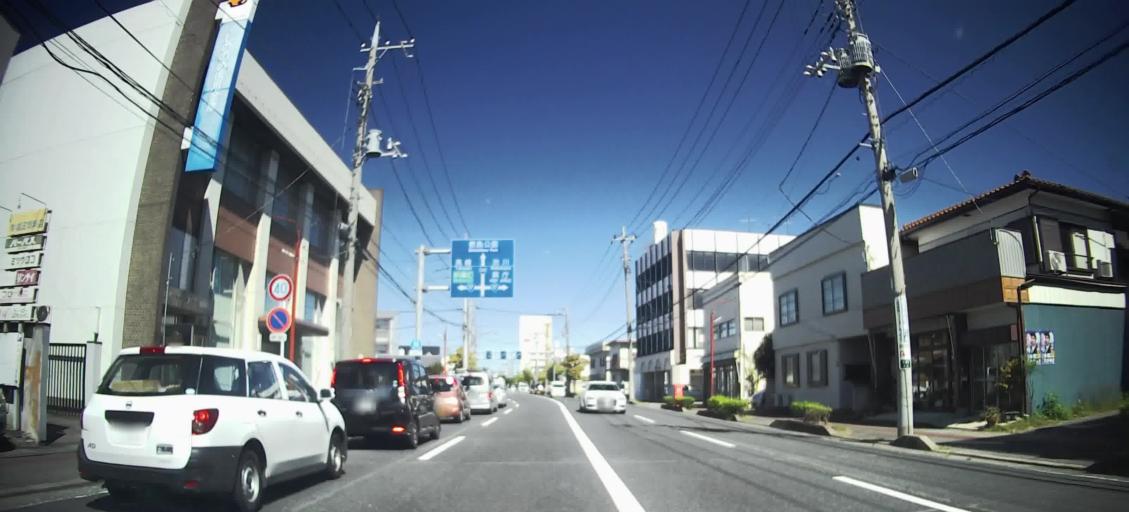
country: JP
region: Gunma
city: Maebashi-shi
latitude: 36.3849
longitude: 139.0540
